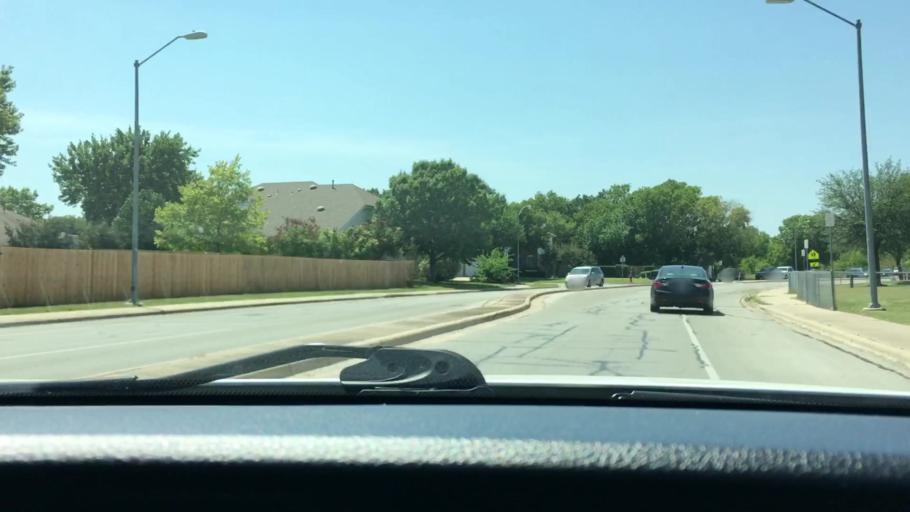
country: US
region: Texas
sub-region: Travis County
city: Windemere
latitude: 30.4668
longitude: -97.6538
